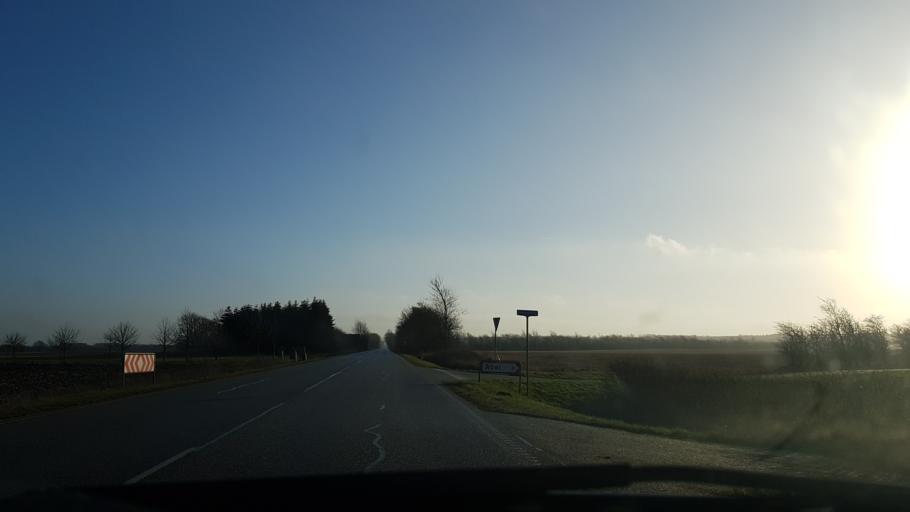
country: DK
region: South Denmark
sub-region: Tonder Kommune
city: Toftlund
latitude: 55.2405
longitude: 9.1593
